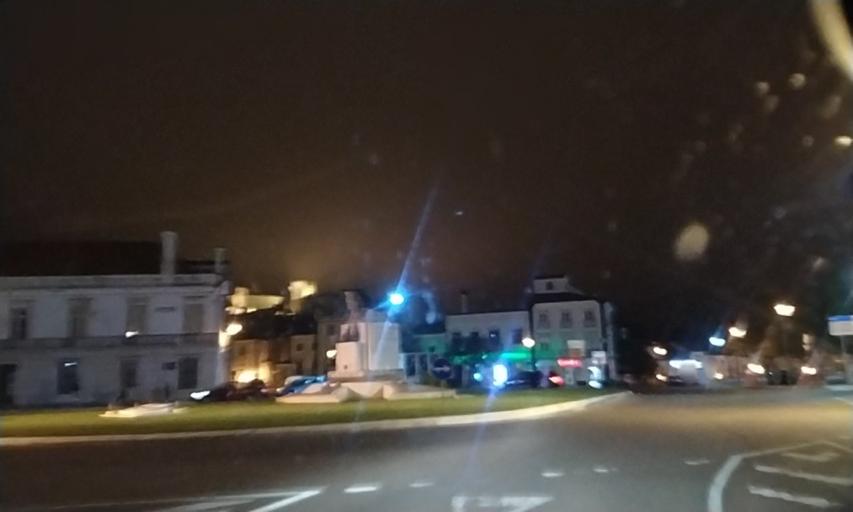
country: PT
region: Evora
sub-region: Estremoz
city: Estremoz
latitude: 38.8434
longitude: -7.5865
